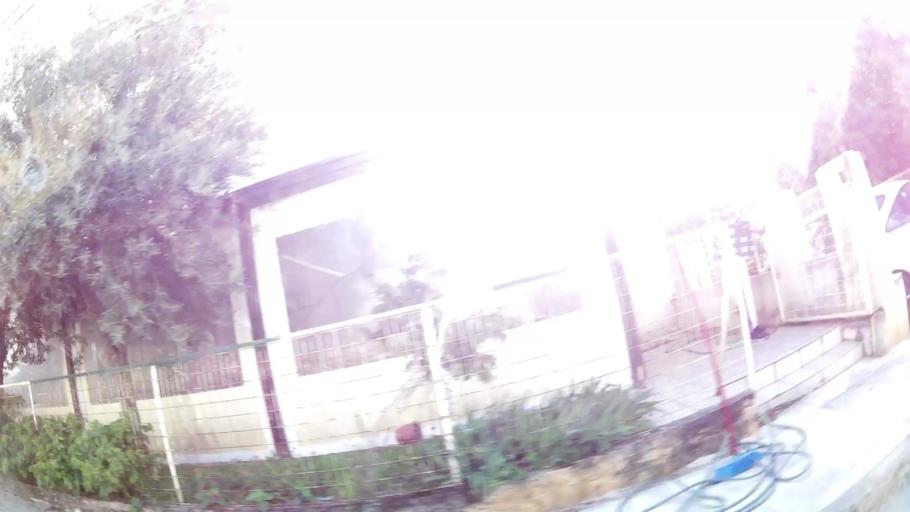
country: GR
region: Attica
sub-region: Nomarchia Athinas
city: Melissia
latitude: 38.0559
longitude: 23.8181
